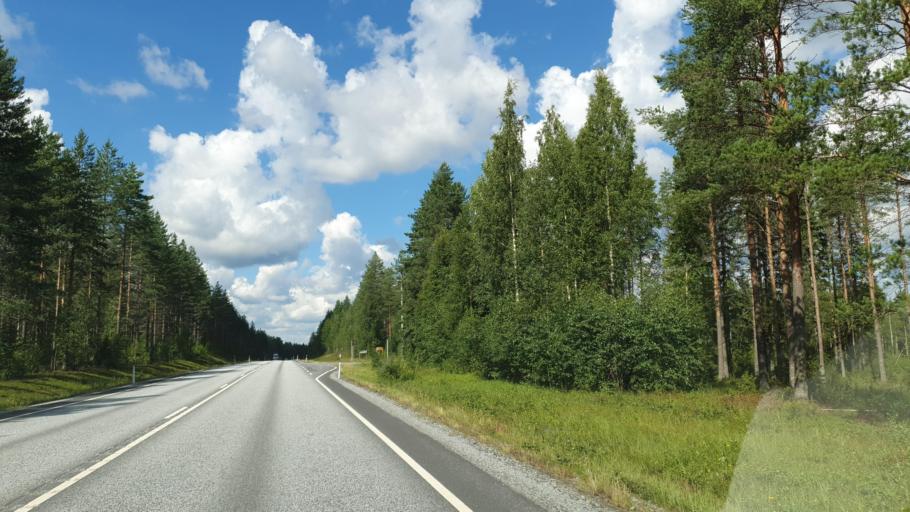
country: FI
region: Northern Savo
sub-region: Ylae-Savo
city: Sonkajaervi
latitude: 63.8946
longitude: 27.4125
